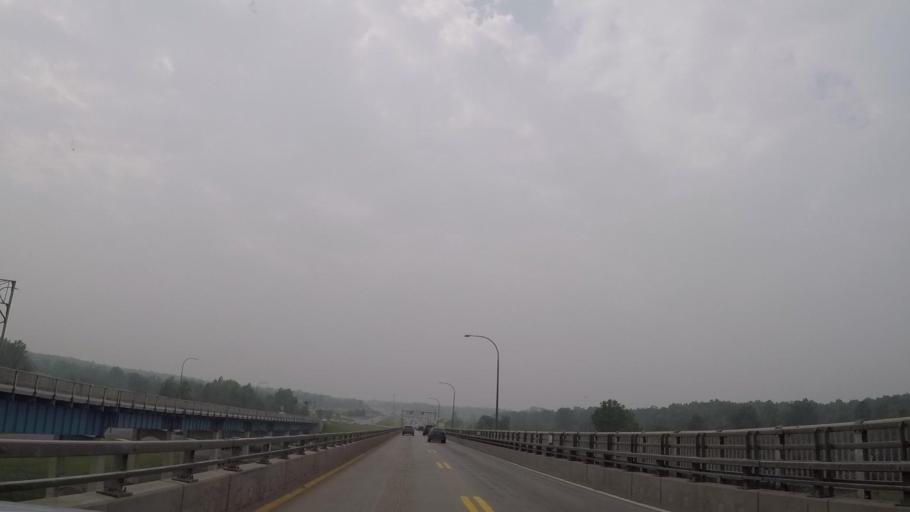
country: US
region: New York
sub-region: Erie County
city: Grandyle Village
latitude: 42.9996
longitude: -78.9383
